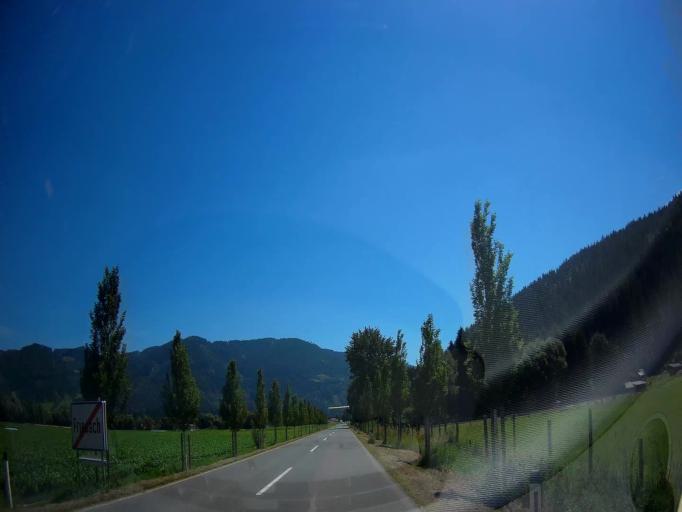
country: AT
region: Carinthia
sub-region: Politischer Bezirk Sankt Veit an der Glan
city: Friesach
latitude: 46.9454
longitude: 14.4141
